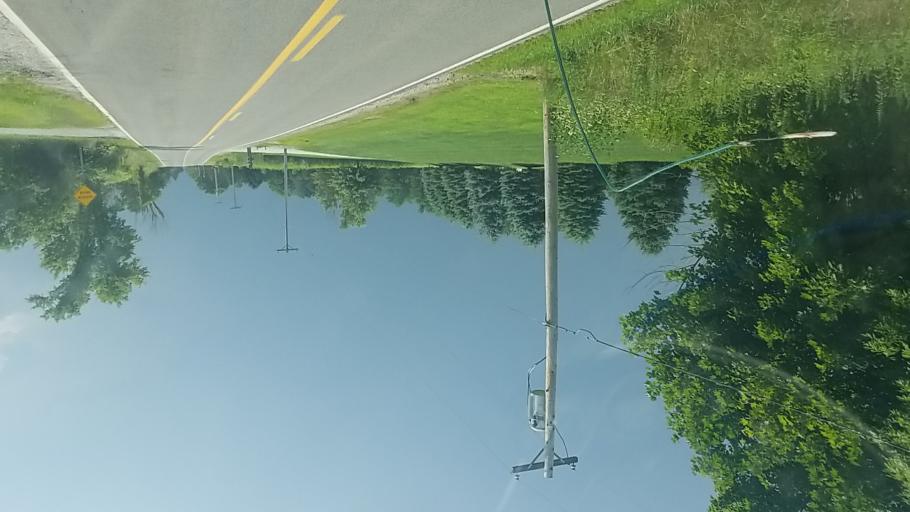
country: US
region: Ohio
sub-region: Medina County
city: Lodi
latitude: 41.0683
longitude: -82.0051
